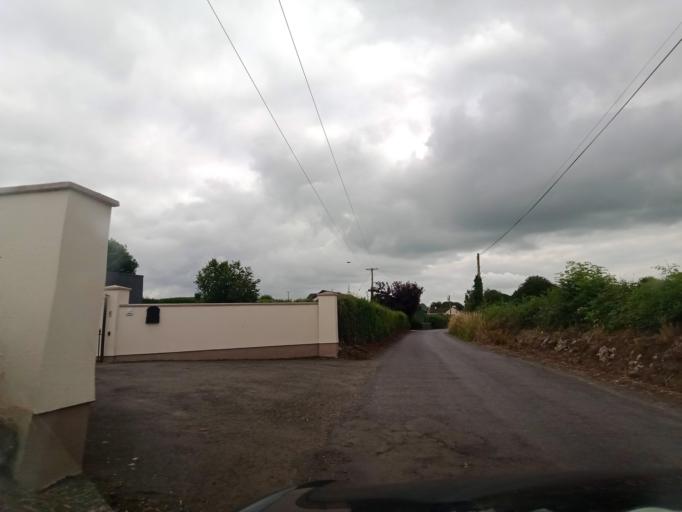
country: IE
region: Leinster
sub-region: Laois
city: Stradbally
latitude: 52.9783
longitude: -7.1615
